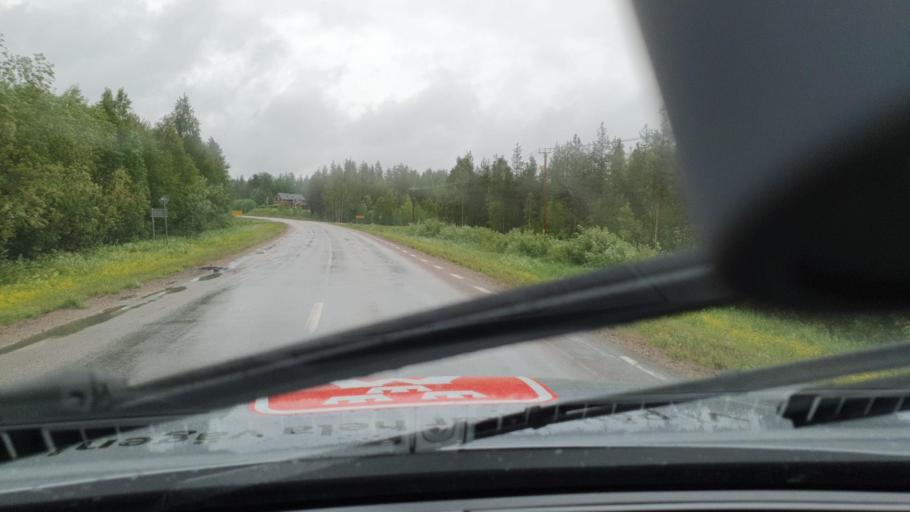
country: SE
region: Norrbotten
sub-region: Overkalix Kommun
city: OEverkalix
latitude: 66.4381
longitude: 23.1979
